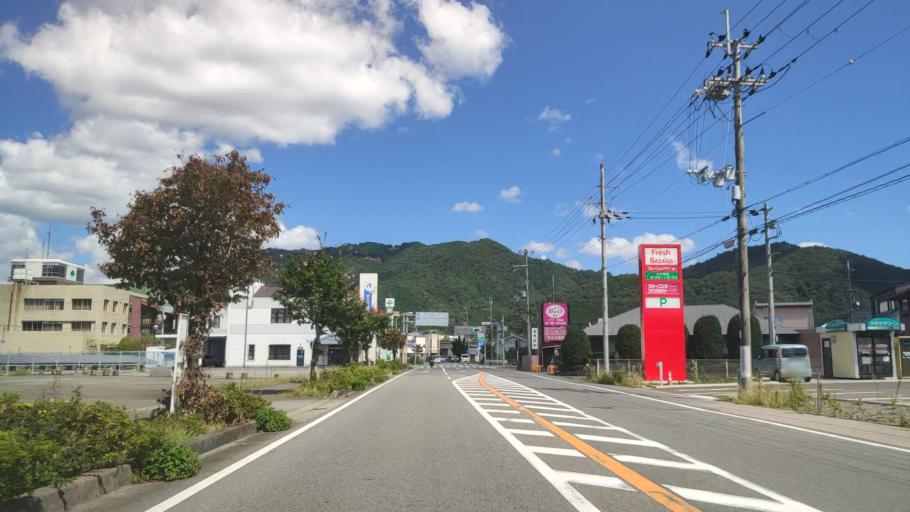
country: JP
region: Kyoto
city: Fukuchiyama
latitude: 35.2088
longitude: 135.1345
